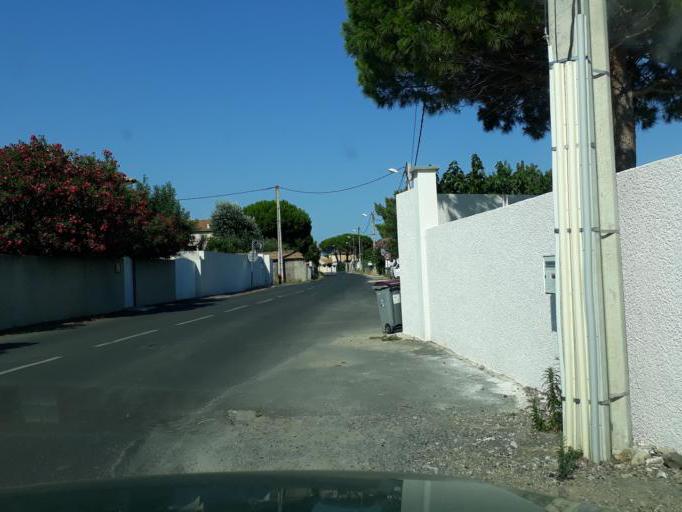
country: FR
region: Languedoc-Roussillon
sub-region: Departement de l'Herault
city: Agde
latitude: 43.2903
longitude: 3.4492
